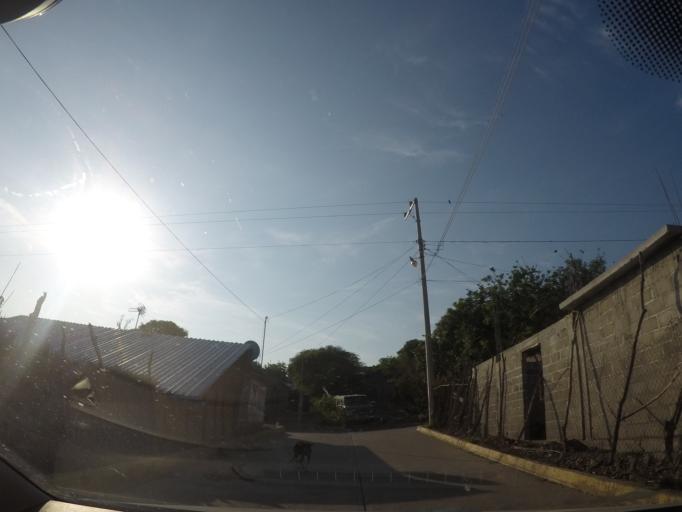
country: MX
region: Oaxaca
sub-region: Santo Domingo Tehuantepec
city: La Noria
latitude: 16.2457
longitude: -95.1473
